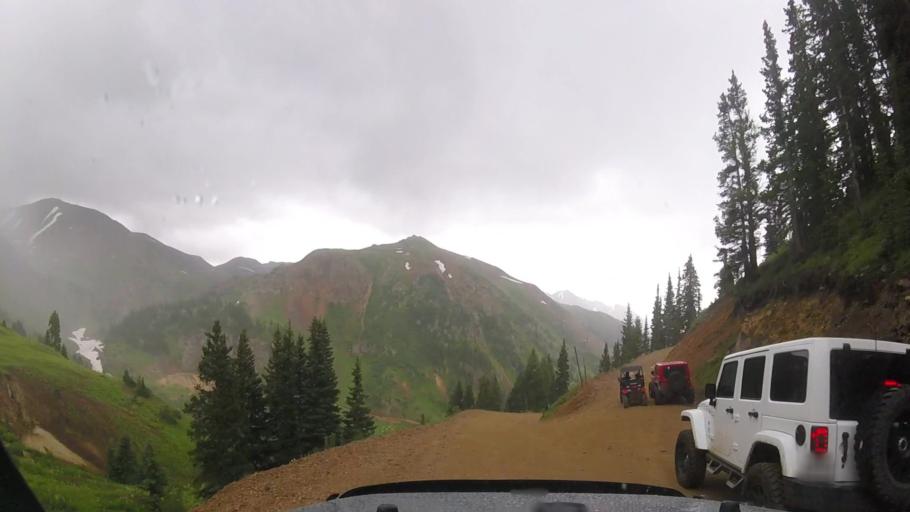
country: US
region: Colorado
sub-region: San Juan County
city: Silverton
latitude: 37.9104
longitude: -107.6454
